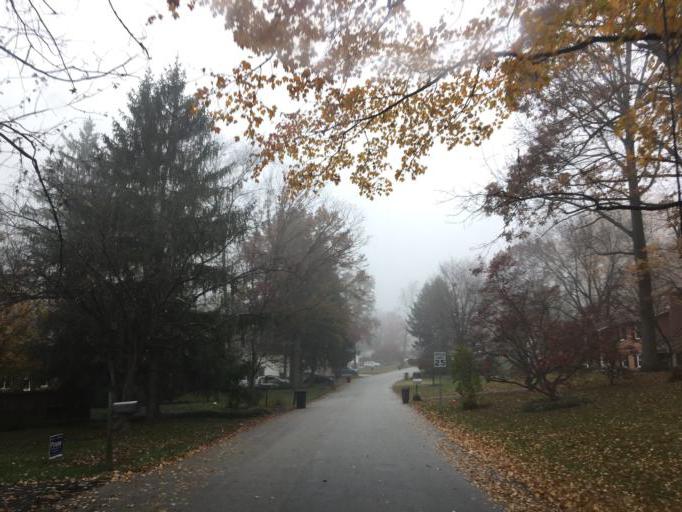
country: US
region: Maryland
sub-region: Howard County
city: Riverside
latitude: 39.1844
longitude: -76.8570
